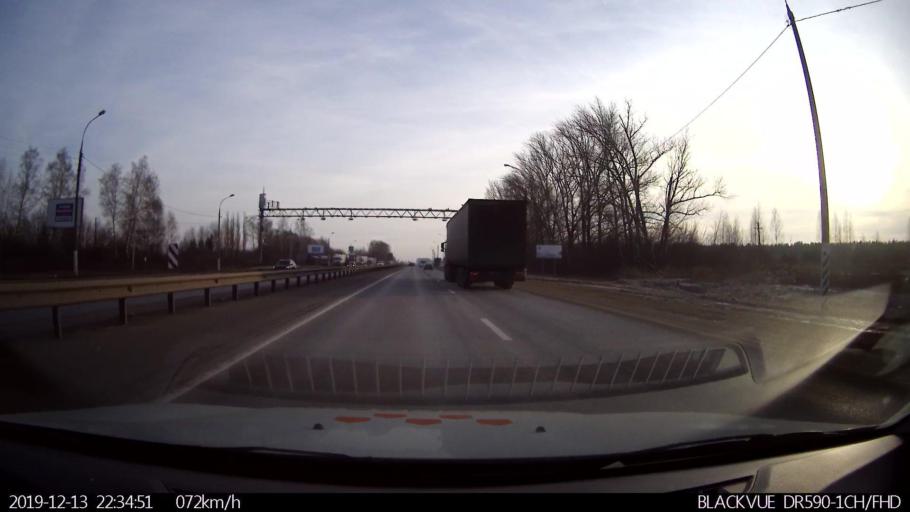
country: RU
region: Nizjnij Novgorod
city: Kstovo
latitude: 56.1888
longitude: 44.1368
